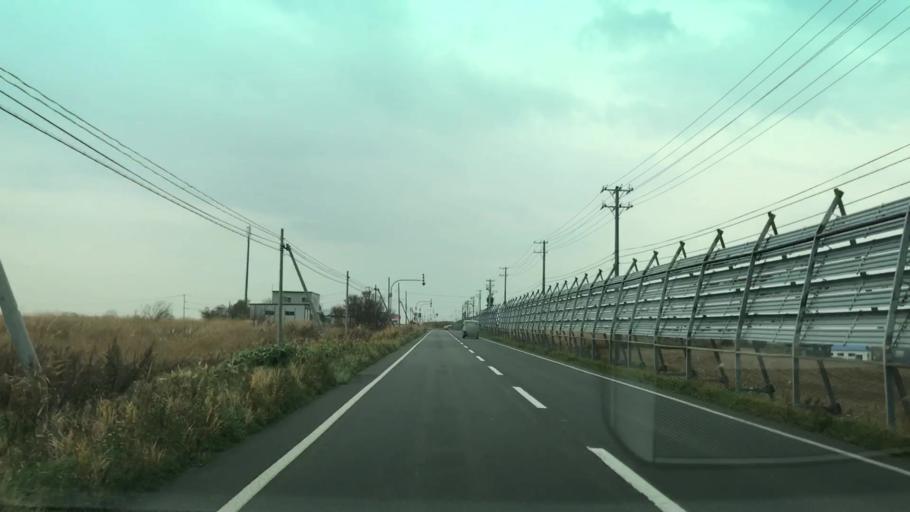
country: JP
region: Hokkaido
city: Ishikari
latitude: 43.2847
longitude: 141.4098
